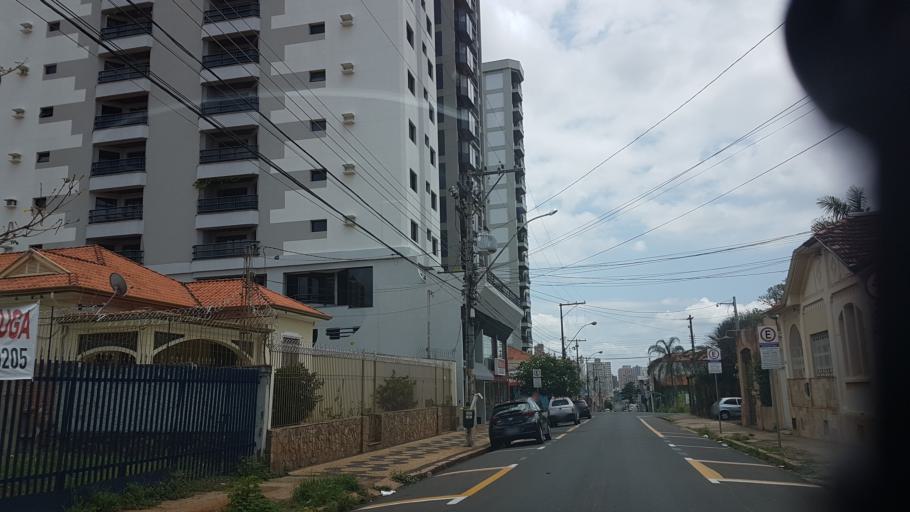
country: BR
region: Sao Paulo
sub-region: Piracicaba
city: Piracicaba
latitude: -22.7351
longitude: -47.6525
